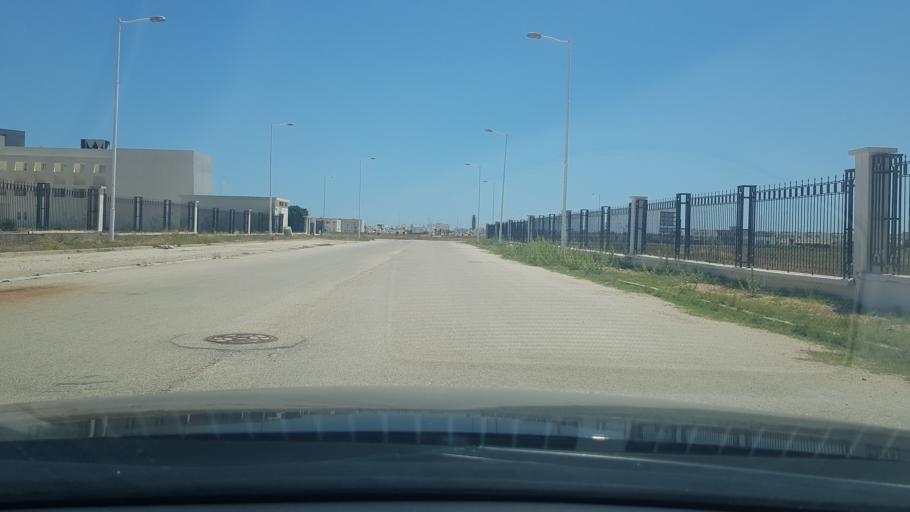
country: TN
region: Safaqis
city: Al Qarmadah
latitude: 34.8366
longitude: 10.7519
